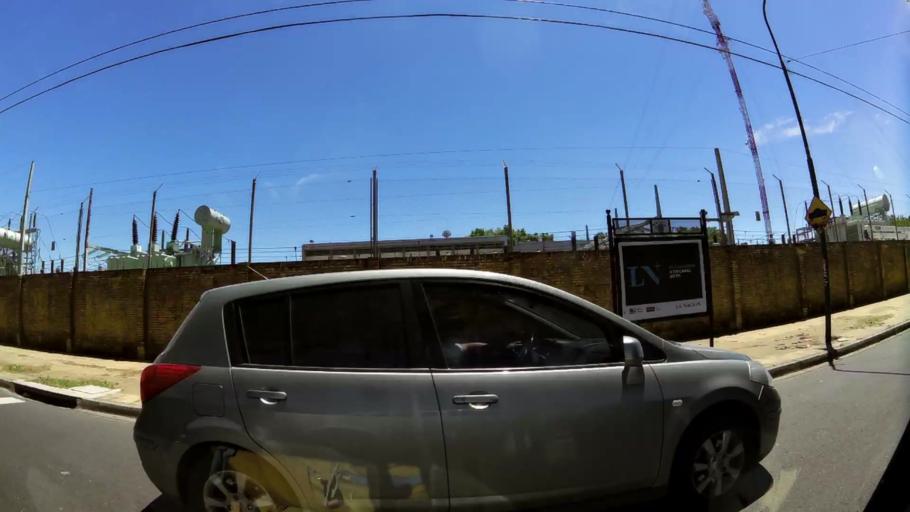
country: AR
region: Buenos Aires
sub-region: Partido de Vicente Lopez
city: Olivos
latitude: -34.5000
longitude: -58.5145
